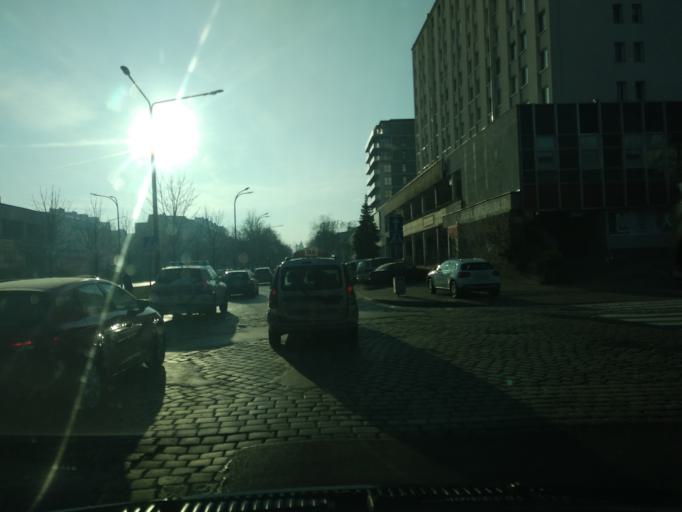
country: PL
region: Lower Silesian Voivodeship
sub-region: Powiat wroclawski
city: Wroclaw
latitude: 51.0952
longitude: 17.0150
